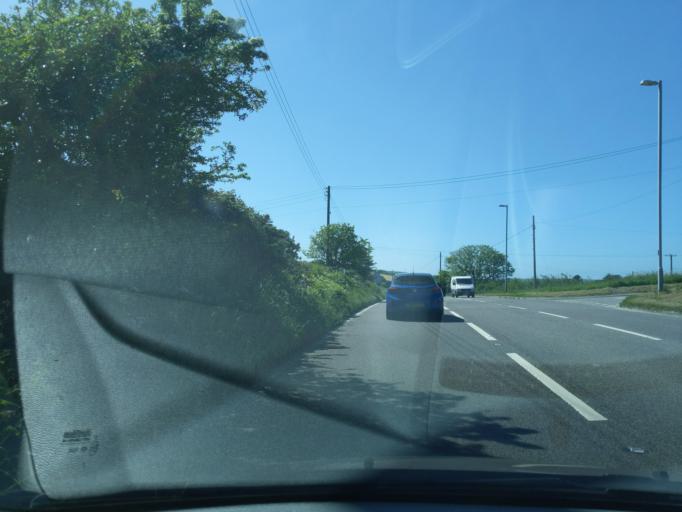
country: GB
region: England
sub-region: Cornwall
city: Penryn
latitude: 50.1647
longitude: -5.1624
